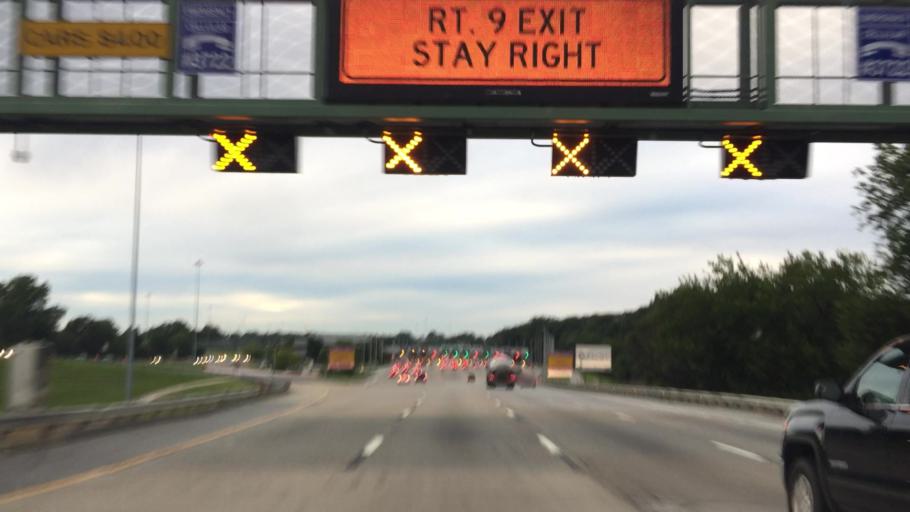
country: US
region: Delaware
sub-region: New Castle County
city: New Castle
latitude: 39.6957
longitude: -75.5404
